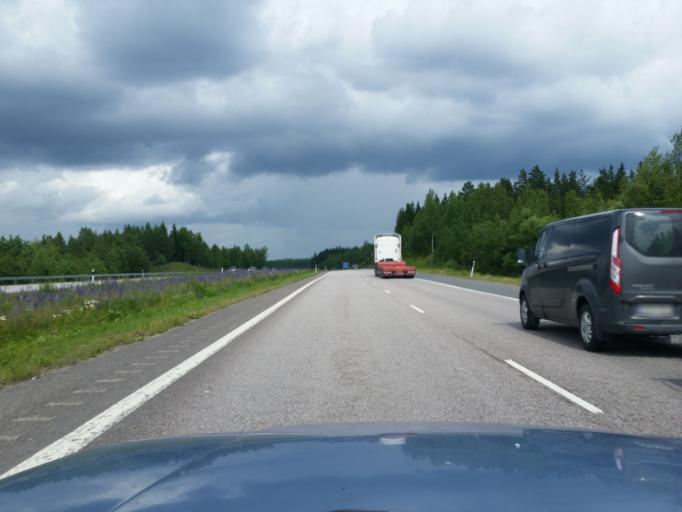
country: FI
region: Paijanne Tavastia
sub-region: Lahti
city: Nastola
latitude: 61.0301
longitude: 25.8372
